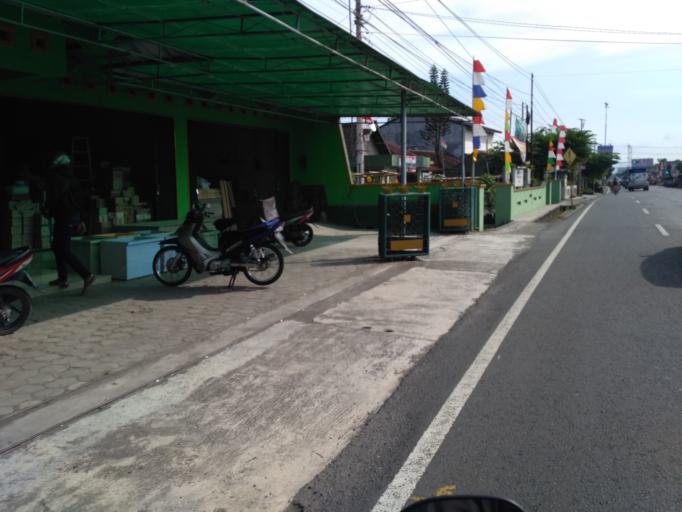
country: ID
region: Daerah Istimewa Yogyakarta
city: Godean
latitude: -7.8121
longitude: 110.2728
